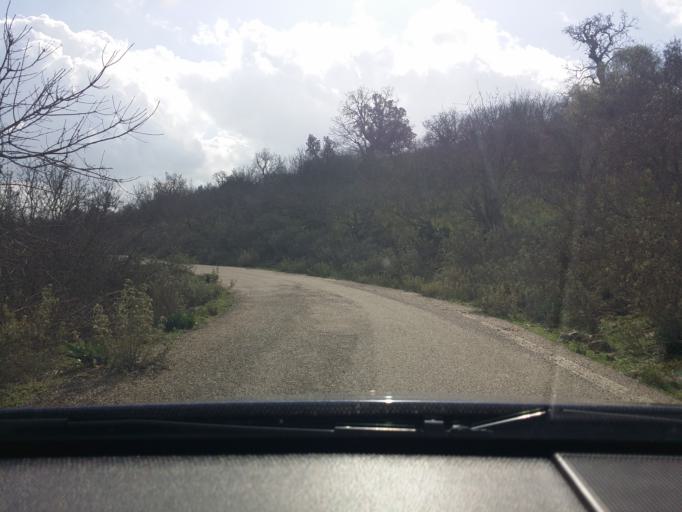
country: GR
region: West Greece
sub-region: Nomos Aitolias kai Akarnanias
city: Fitiai
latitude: 38.6384
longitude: 21.1961
